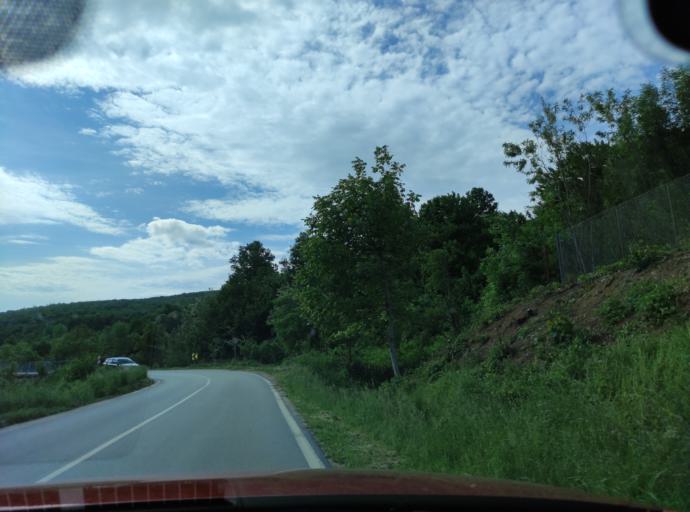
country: BG
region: Montana
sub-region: Obshtina Chiprovtsi
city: Chiprovtsi
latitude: 43.4673
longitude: 22.8665
